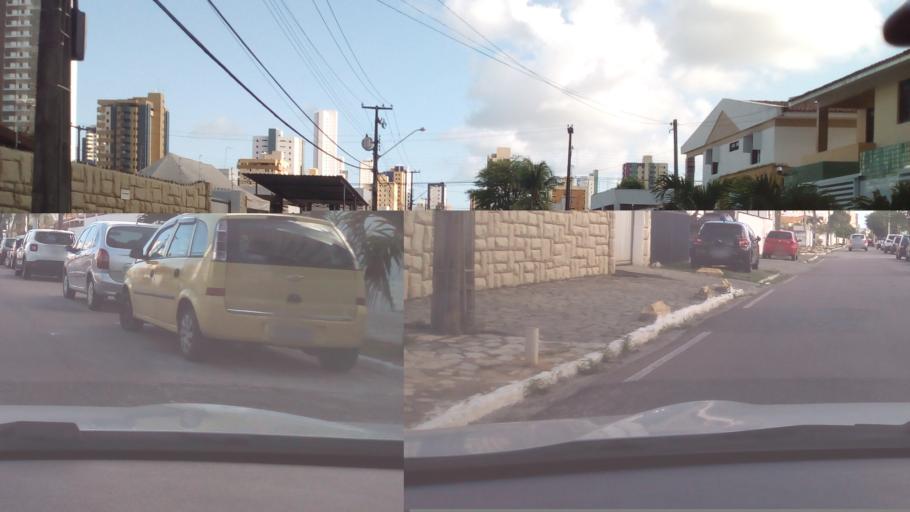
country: BR
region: Paraiba
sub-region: Joao Pessoa
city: Joao Pessoa
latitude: -7.1017
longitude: -34.8404
